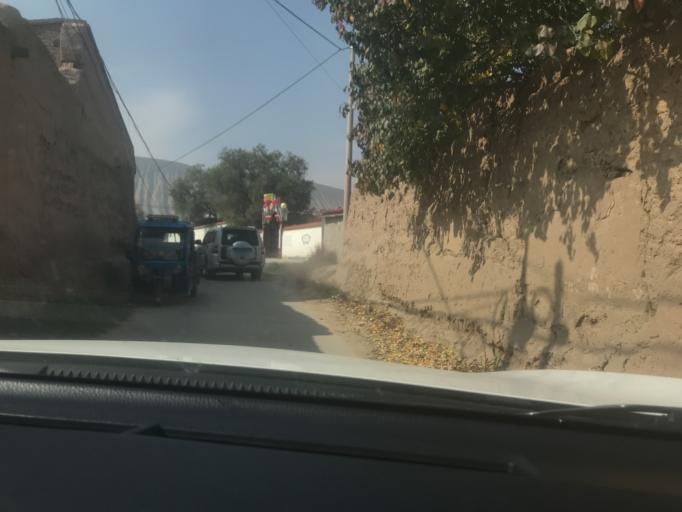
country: CN
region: Gansu Sheng
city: Gulang
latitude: 37.5341
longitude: 102.8783
